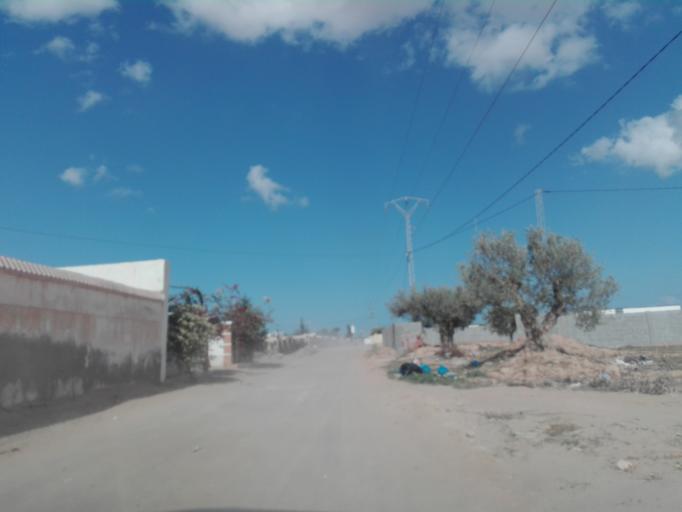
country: TN
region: Madanin
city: Bin Qirdan
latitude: 33.1535
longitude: 11.1935
